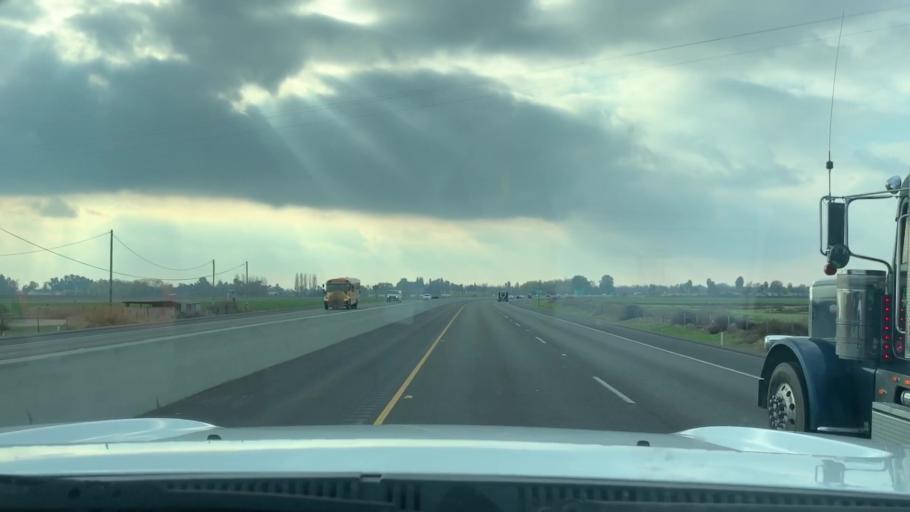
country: US
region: California
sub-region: Kings County
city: Lemoore
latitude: 36.2940
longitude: -119.7628
